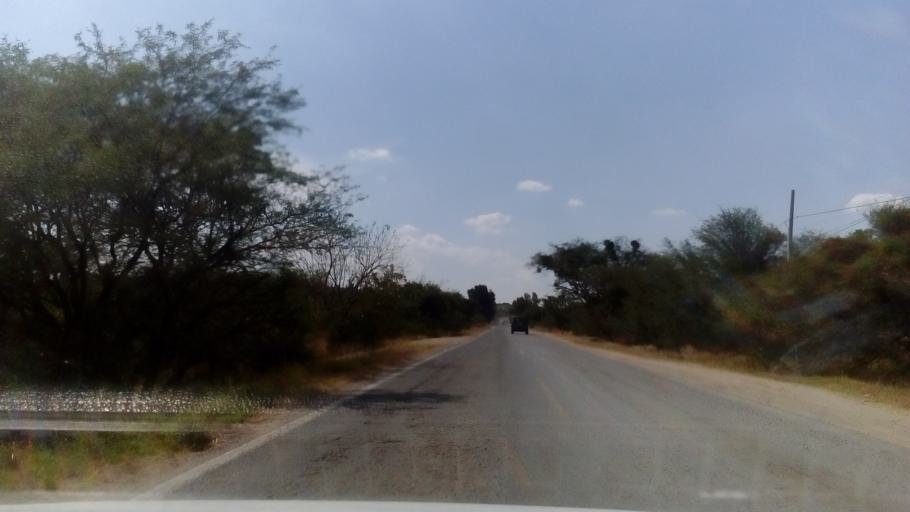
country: MX
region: Guanajuato
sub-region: Silao de la Victoria
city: San Francisco (Banos de Agua Caliente)
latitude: 21.0772
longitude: -101.4753
